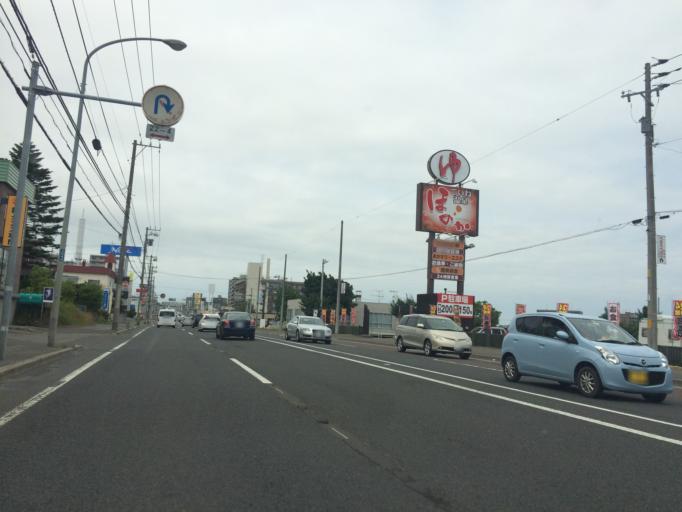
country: JP
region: Hokkaido
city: Sapporo
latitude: 43.1041
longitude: 141.2517
